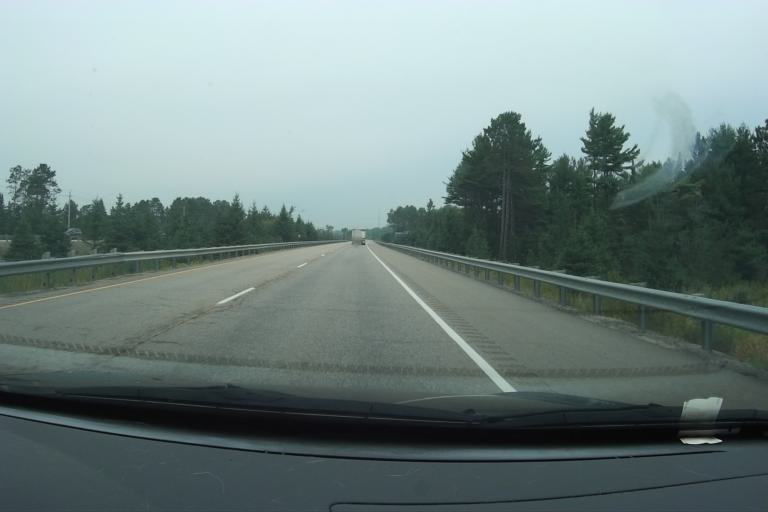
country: CA
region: Ontario
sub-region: Nipissing District
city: North Bay
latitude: 46.2556
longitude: -79.3785
